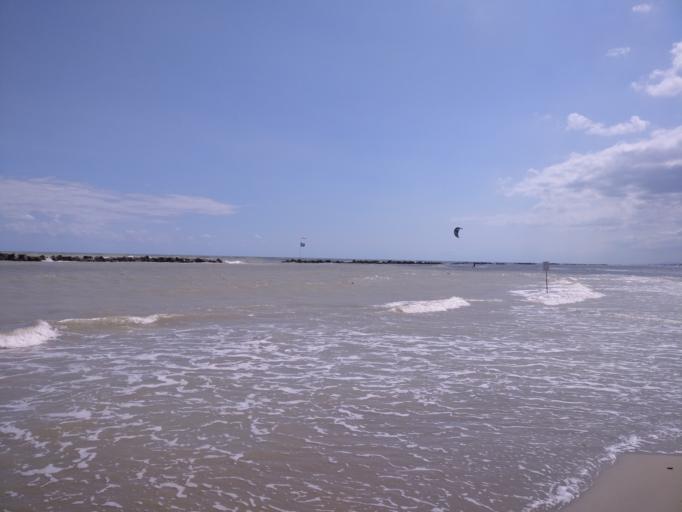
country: IT
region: The Marches
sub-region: Provincia di Ascoli Piceno
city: Cupra Marittima
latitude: 43.0215
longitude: 13.8623
